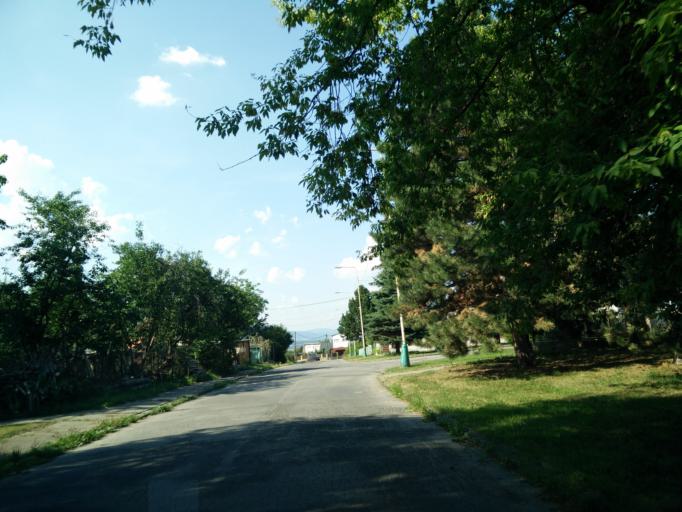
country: SK
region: Nitriansky
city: Prievidza
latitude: 48.7732
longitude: 18.6360
